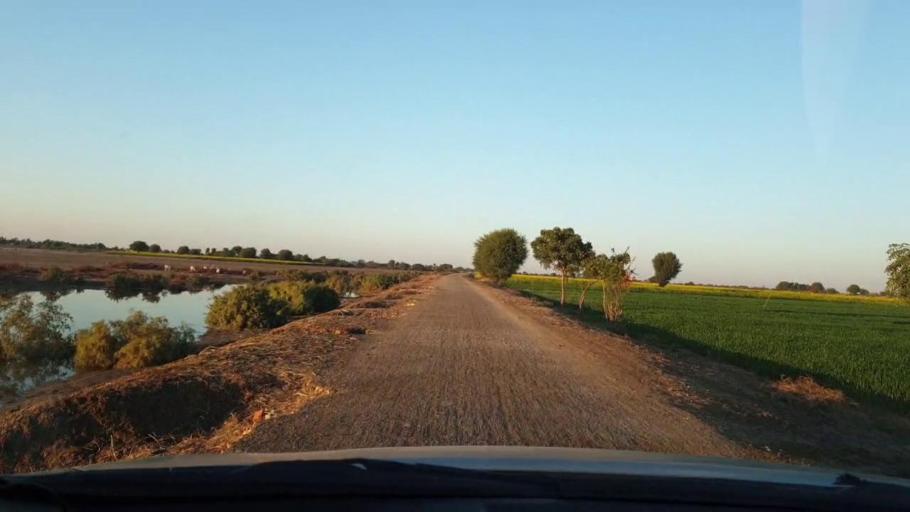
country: PK
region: Sindh
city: Jhol
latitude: 25.8830
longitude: 68.8953
